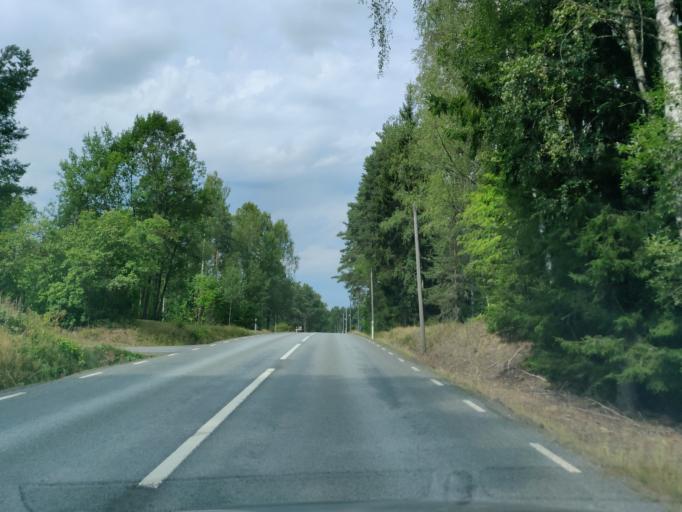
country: SE
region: Vaermland
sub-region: Munkfors Kommun
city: Munkfors
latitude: 59.8860
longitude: 13.5658
